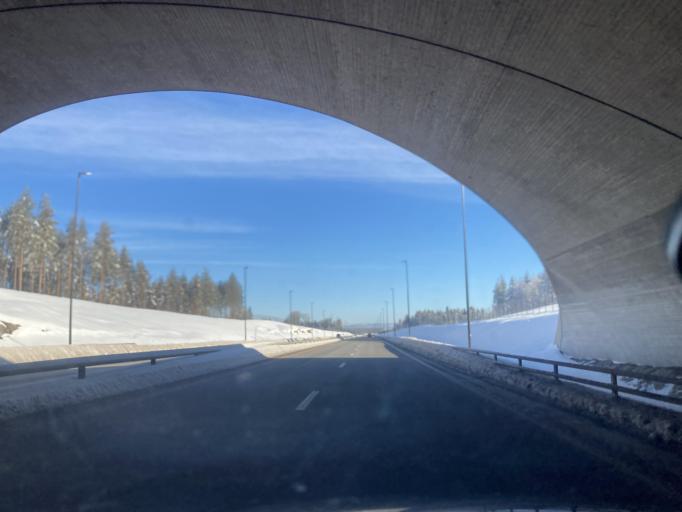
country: NO
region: Hedmark
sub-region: Loten
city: Loten
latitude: 60.8604
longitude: 11.4129
